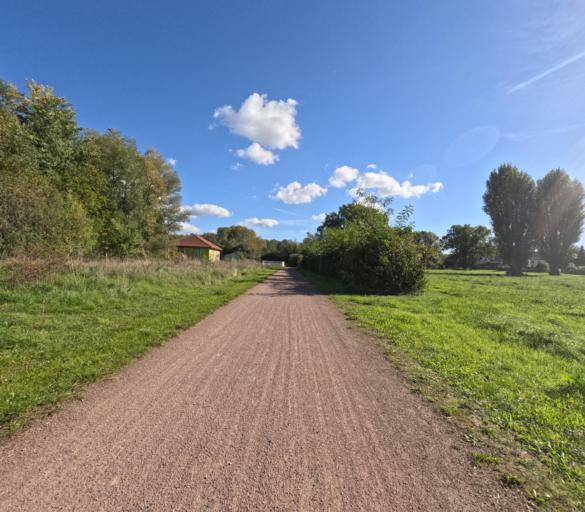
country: DE
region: Saxony
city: Moritzburg
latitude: 51.1262
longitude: 13.7249
